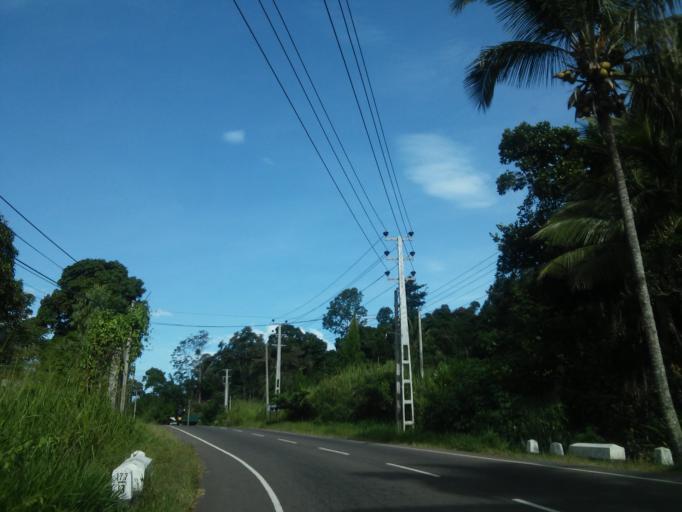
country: LK
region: Uva
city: Haputale
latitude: 6.7615
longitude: 80.8846
